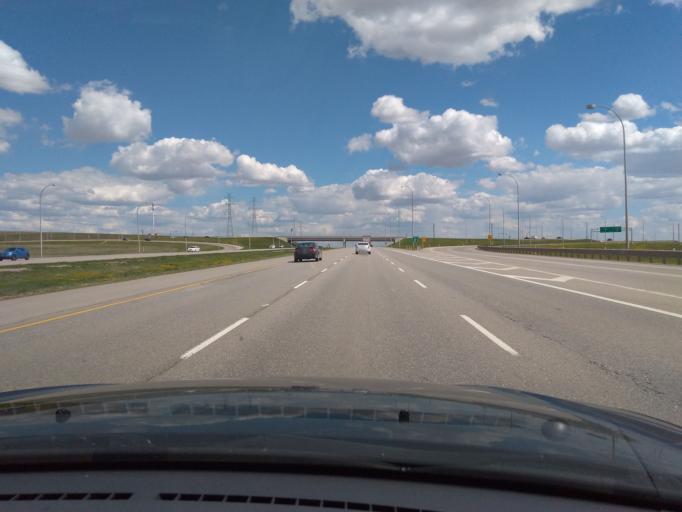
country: CA
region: Alberta
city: Calgary
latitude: 51.1738
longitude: -114.0764
